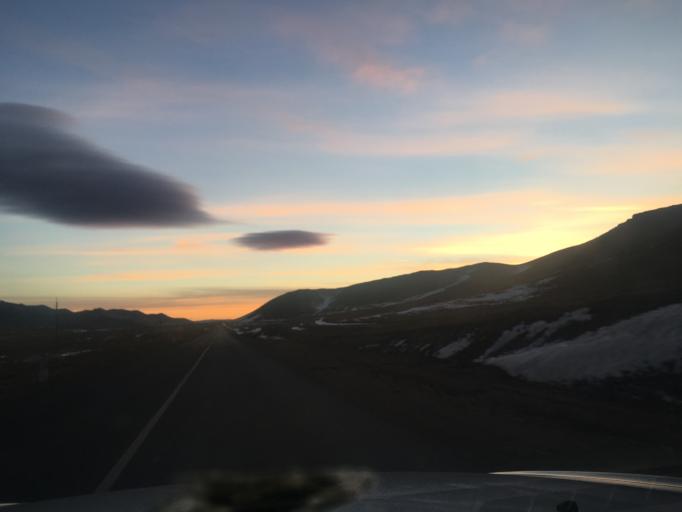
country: MN
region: Central Aimak
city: Mandal
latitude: 48.1181
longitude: 106.6462
